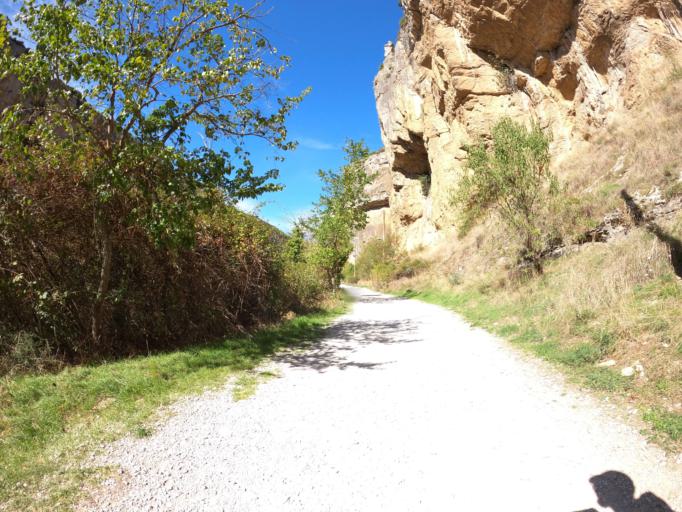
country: ES
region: Navarre
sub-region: Provincia de Navarra
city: Lumbier
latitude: 42.6332
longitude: -1.3022
